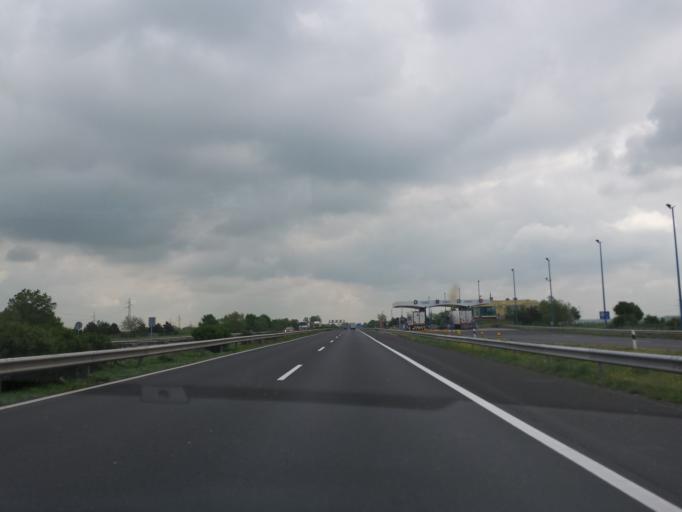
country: HU
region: Gyor-Moson-Sopron
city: Mosonmagyarovar
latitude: 47.8451
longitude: 17.2575
